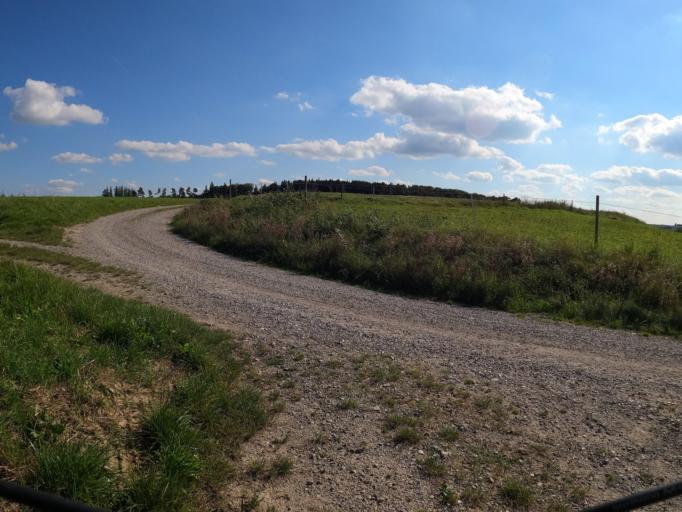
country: DE
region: Bavaria
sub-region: Swabia
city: Roggenburg
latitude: 48.3168
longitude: 10.2481
